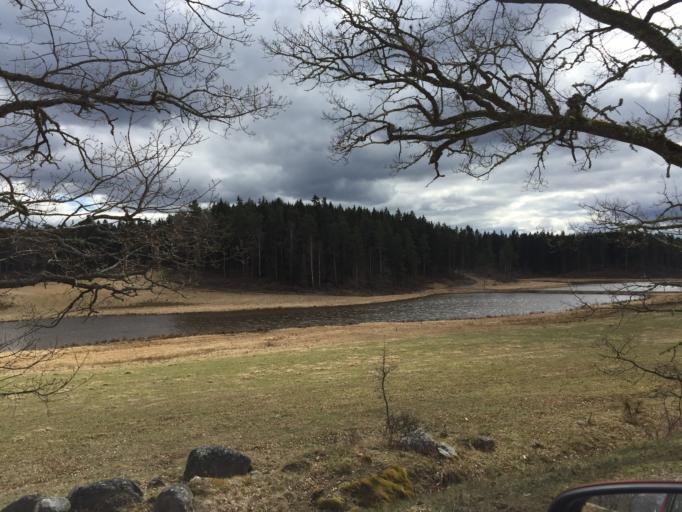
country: SE
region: Soedermanland
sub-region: Nykopings Kommun
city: Nykoping
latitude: 58.9887
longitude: 16.9567
